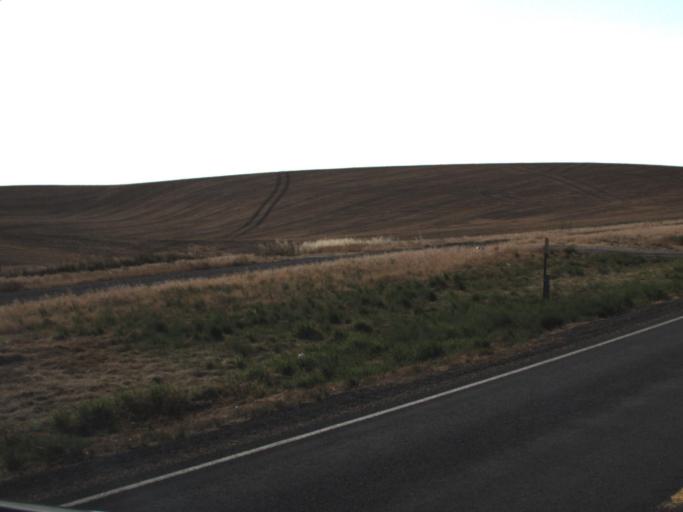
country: US
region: Washington
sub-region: Whitman County
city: Colfax
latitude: 47.1421
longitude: -117.2377
